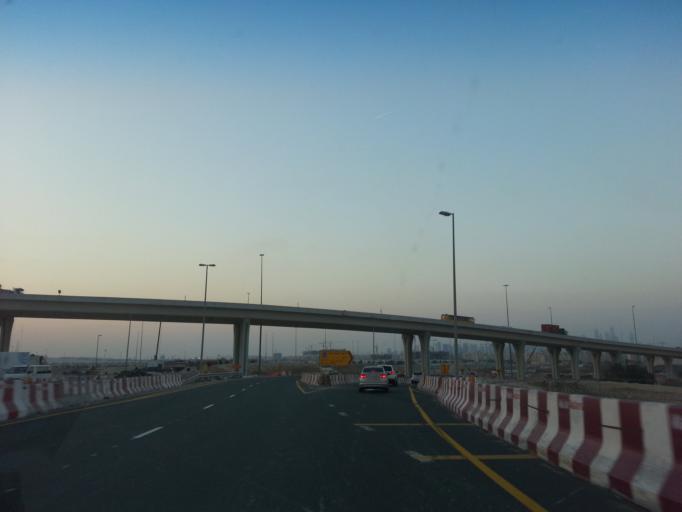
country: AE
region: Dubai
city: Dubai
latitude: 25.0158
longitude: 55.1619
